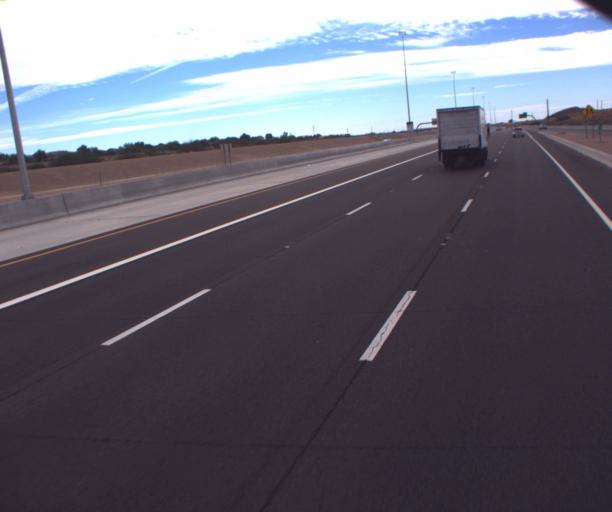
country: US
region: Arizona
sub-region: Pinal County
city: Apache Junction
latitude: 33.4634
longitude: -111.6785
